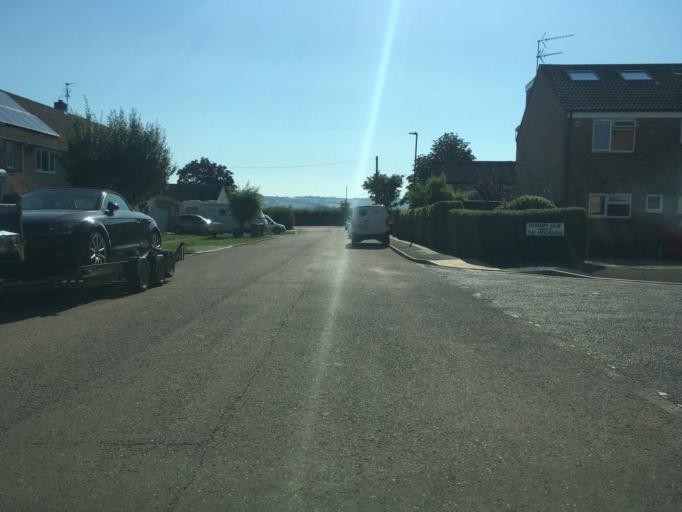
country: GB
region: England
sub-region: South Gloucestershire
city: Pucklechurch
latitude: 51.4809
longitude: -2.4294
